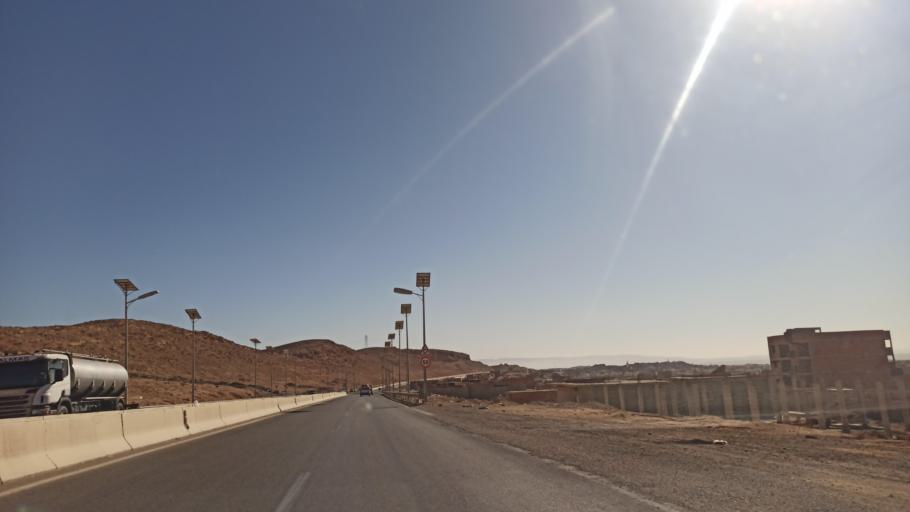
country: TN
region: Gafsa
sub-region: Gafsa Municipality
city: Gafsa
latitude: 34.4461
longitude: 8.7868
